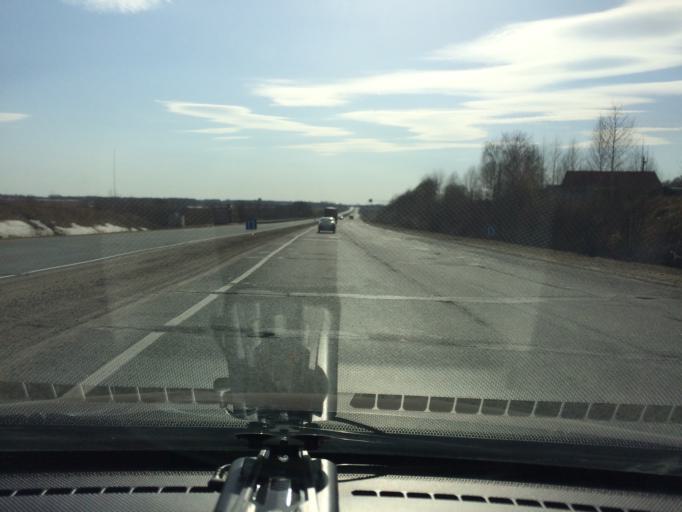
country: RU
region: Mariy-El
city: Yoshkar-Ola
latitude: 56.6900
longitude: 48.0491
